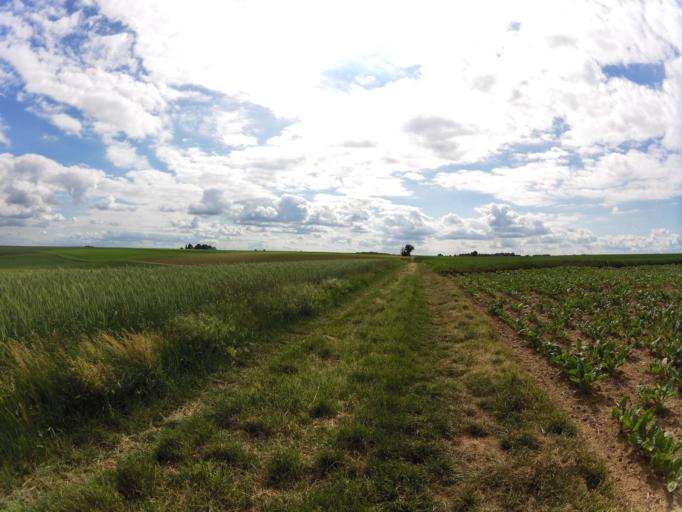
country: DE
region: Bavaria
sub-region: Regierungsbezirk Unterfranken
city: Gaukonigshofen
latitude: 49.6557
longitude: 10.0082
